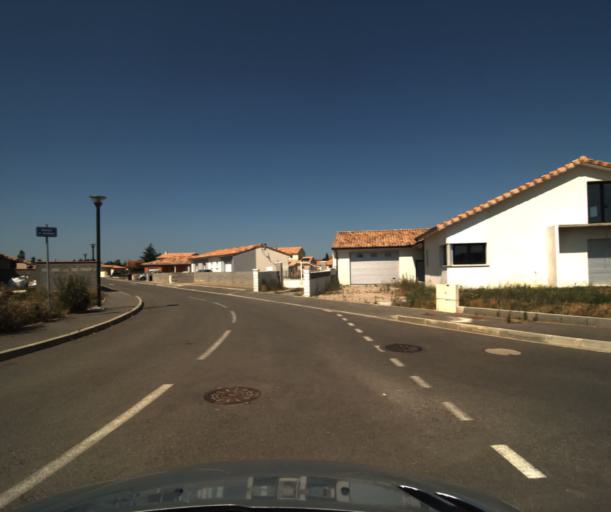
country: FR
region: Midi-Pyrenees
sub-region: Departement de la Haute-Garonne
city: Muret
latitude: 43.4667
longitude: 1.3755
